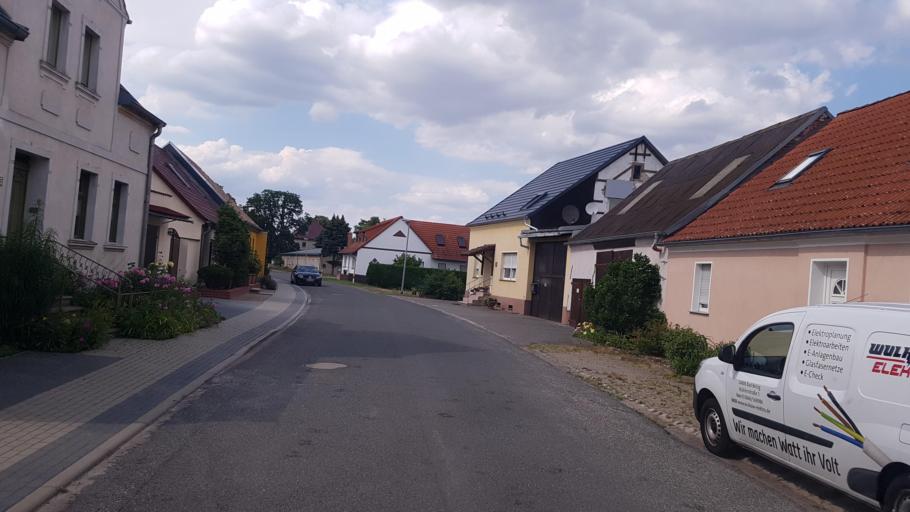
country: DE
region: Brandenburg
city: Golzow
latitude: 52.2443
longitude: 12.5817
